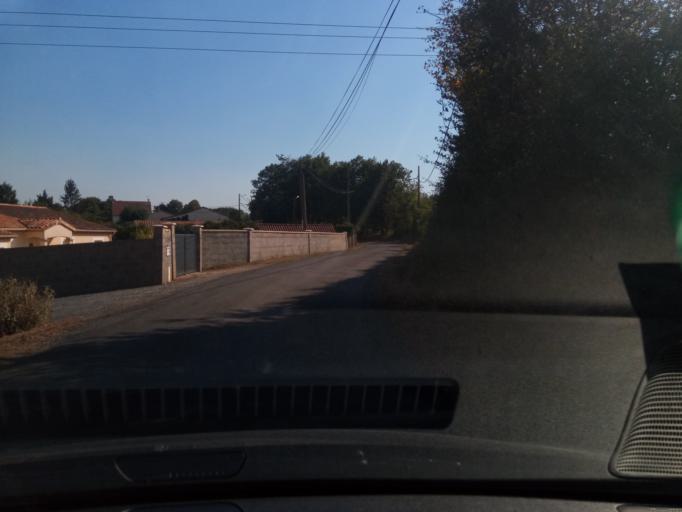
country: FR
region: Poitou-Charentes
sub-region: Departement de la Vienne
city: Montmorillon
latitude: 46.4125
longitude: 0.8765
